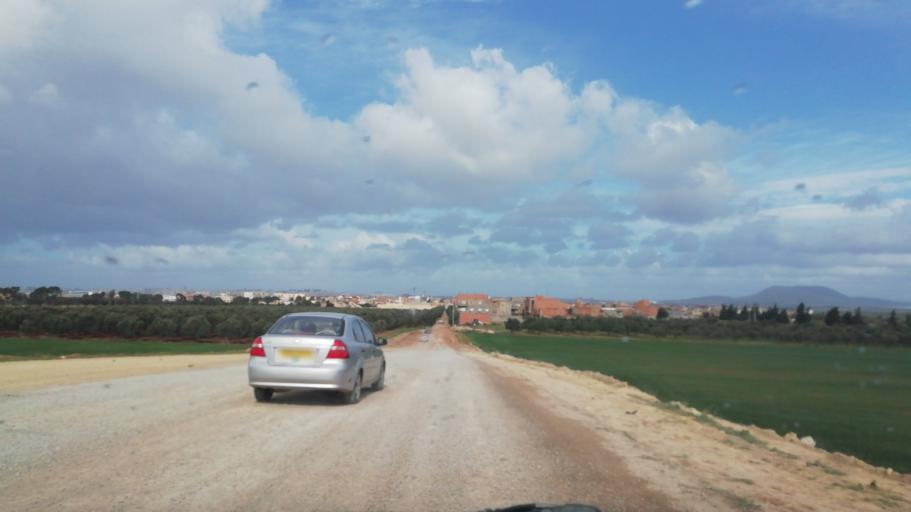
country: DZ
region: Oran
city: Sidi ech Chahmi
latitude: 35.6494
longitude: -0.5182
